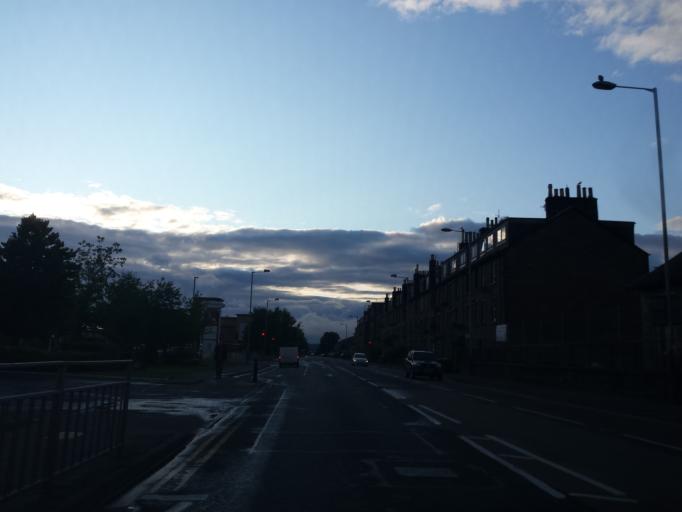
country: GB
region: Scotland
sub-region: Perth and Kinross
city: Perth
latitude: 56.4004
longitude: -3.4379
